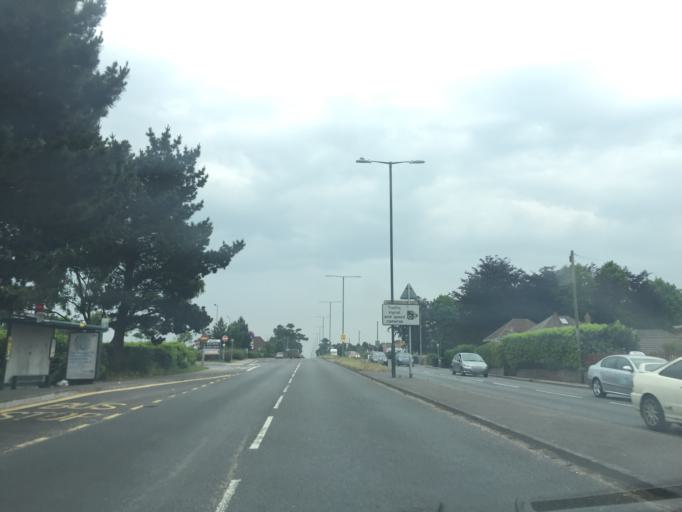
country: GB
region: England
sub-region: Dorset
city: Parkstone
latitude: 50.7581
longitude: -1.9266
